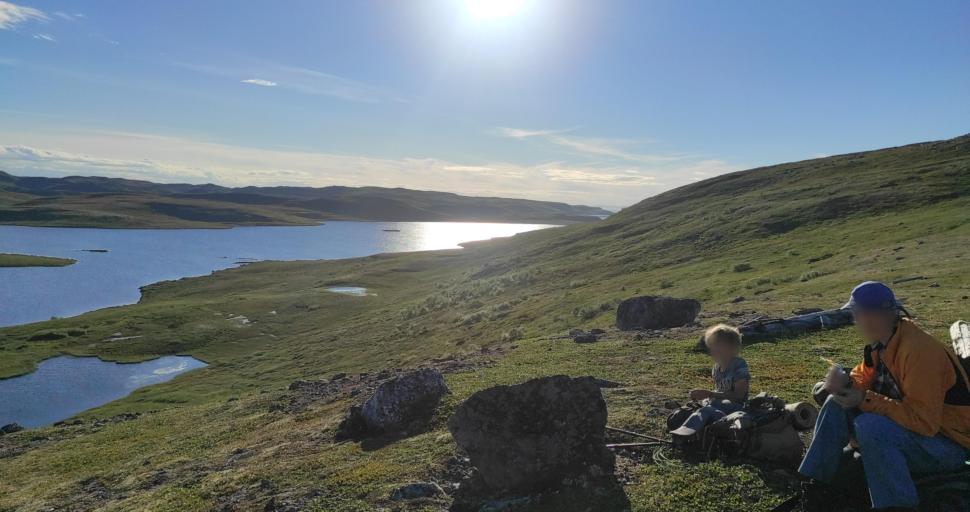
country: RU
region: Murmansk
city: Teriberka
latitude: 69.1798
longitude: 35.4659
